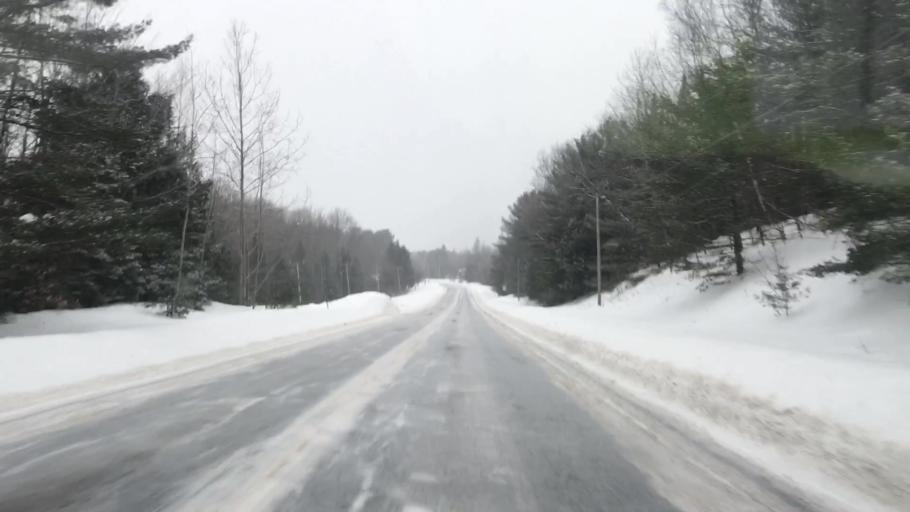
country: US
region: Maine
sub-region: Penobscot County
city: Medway
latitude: 45.5404
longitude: -68.3684
